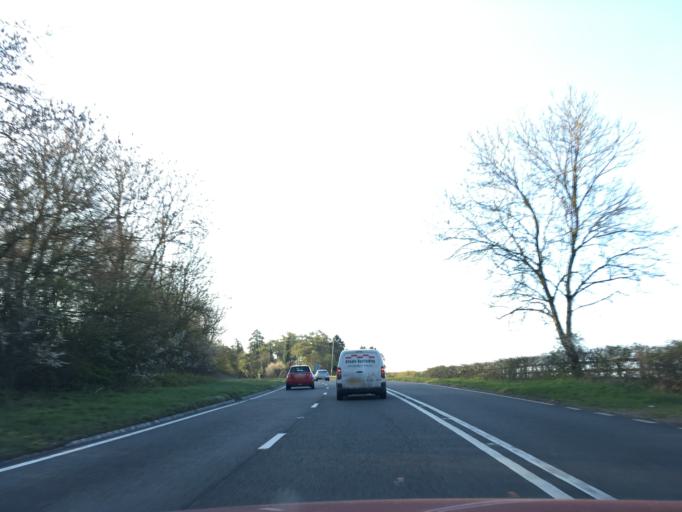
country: GB
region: England
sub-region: Gloucestershire
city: Shipton Village
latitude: 51.8620
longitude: -1.9575
